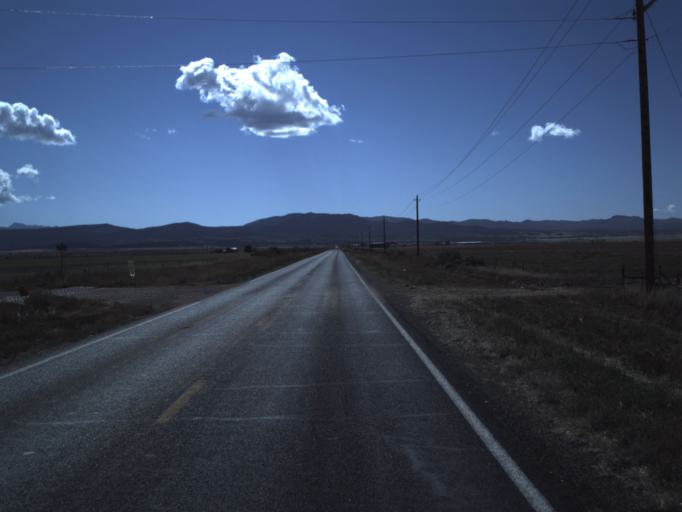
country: US
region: Utah
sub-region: Washington County
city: Enterprise
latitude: 37.6416
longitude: -113.6612
